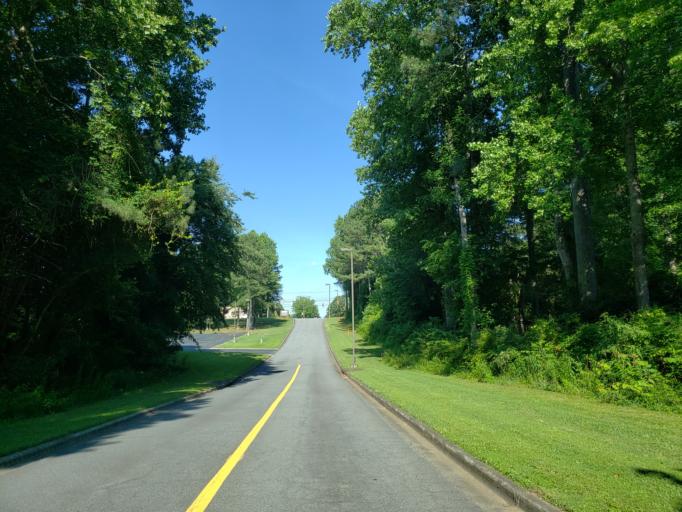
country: US
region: Georgia
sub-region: Cherokee County
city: Woodstock
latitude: 34.1286
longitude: -84.5882
